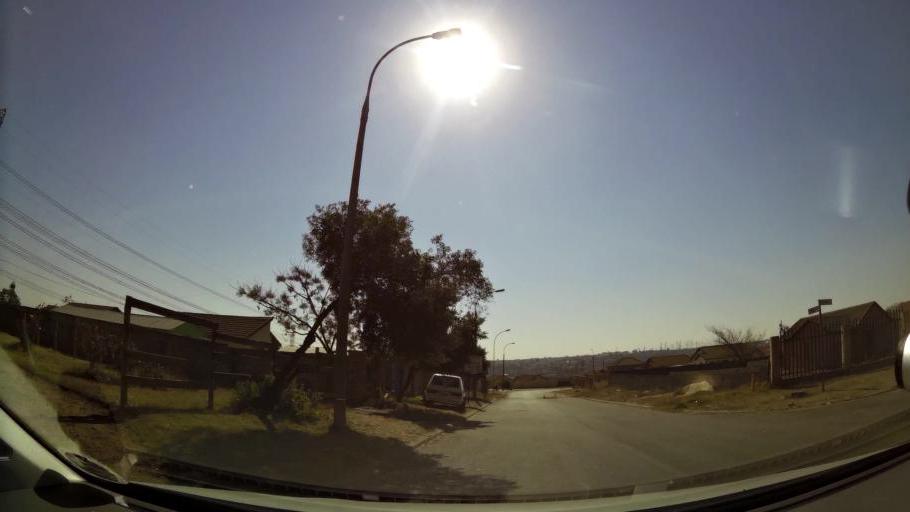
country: ZA
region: Gauteng
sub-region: Ekurhuleni Metropolitan Municipality
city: Tembisa
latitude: -26.0391
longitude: 28.2133
